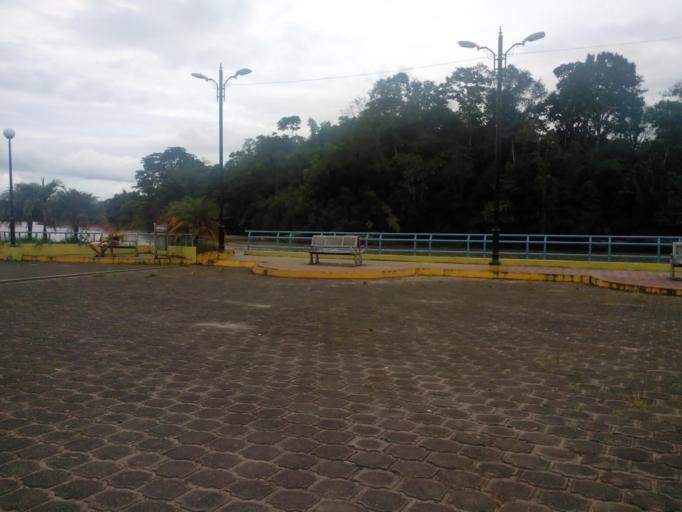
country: EC
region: Napo
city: Tena
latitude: -1.0356
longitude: -77.6659
